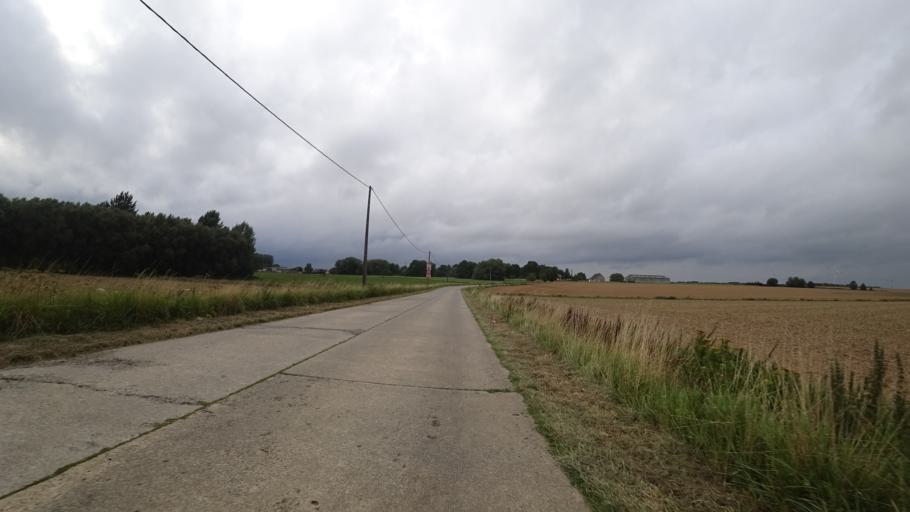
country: BE
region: Wallonia
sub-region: Province du Brabant Wallon
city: Perwez
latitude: 50.5704
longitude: 4.7804
